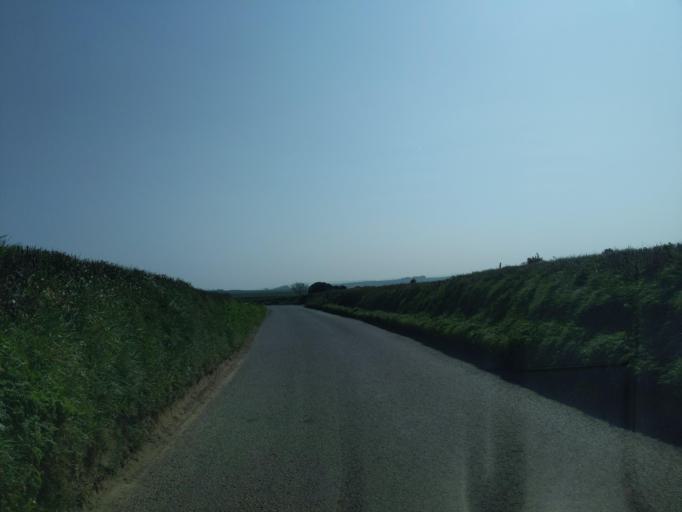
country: GB
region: England
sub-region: Devon
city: Dartmouth
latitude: 50.3415
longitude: -3.6542
